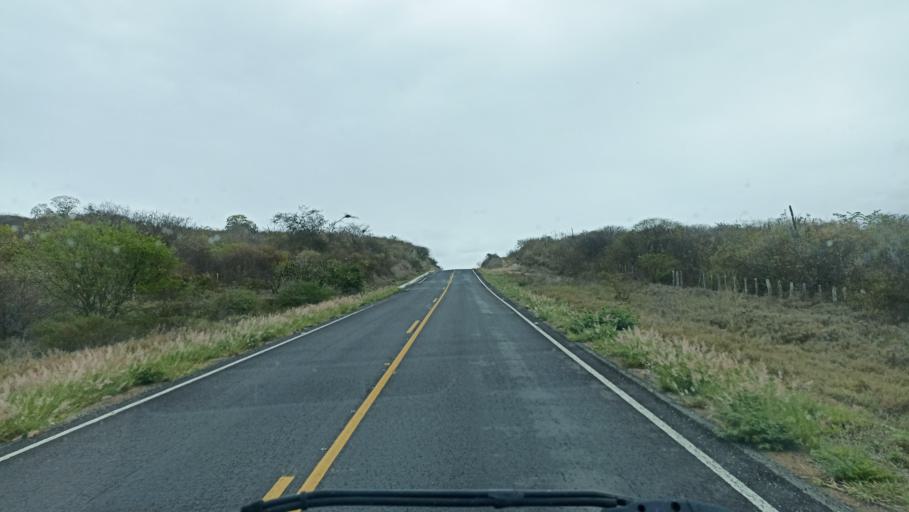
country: BR
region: Bahia
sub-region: Andarai
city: Vera Cruz
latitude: -13.0467
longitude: -40.7659
